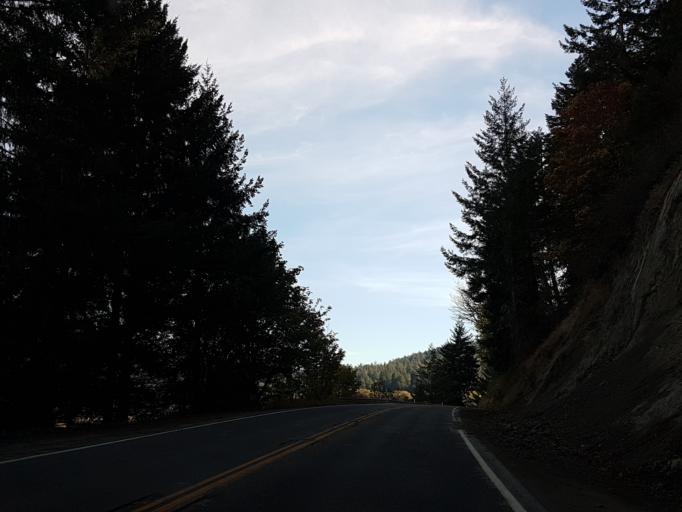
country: US
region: California
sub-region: Humboldt County
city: Rio Dell
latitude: 40.4266
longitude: -123.9814
